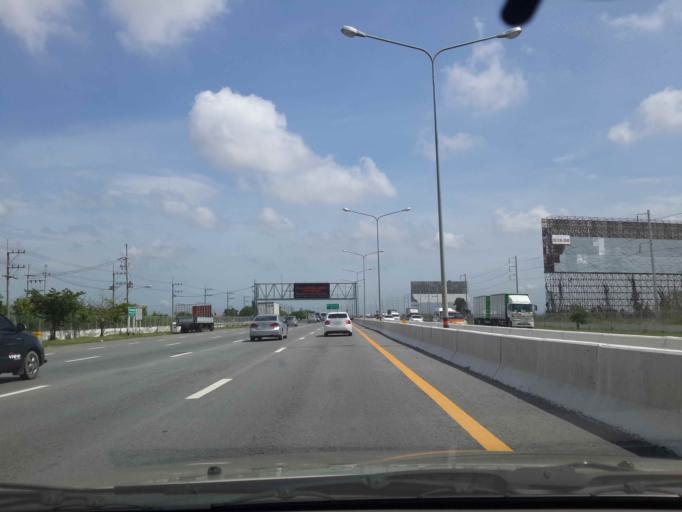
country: TH
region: Chachoengsao
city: Bang Pakong
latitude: 13.5873
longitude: 100.9683
